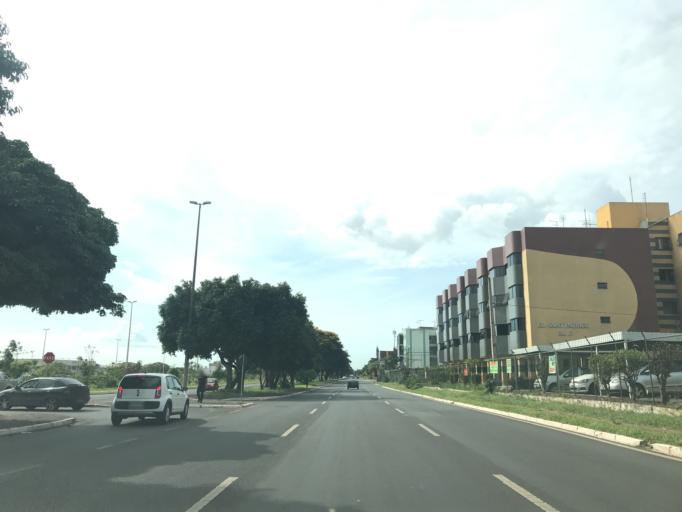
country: BR
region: Federal District
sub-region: Brasilia
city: Brasilia
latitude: -15.8219
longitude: -48.0862
